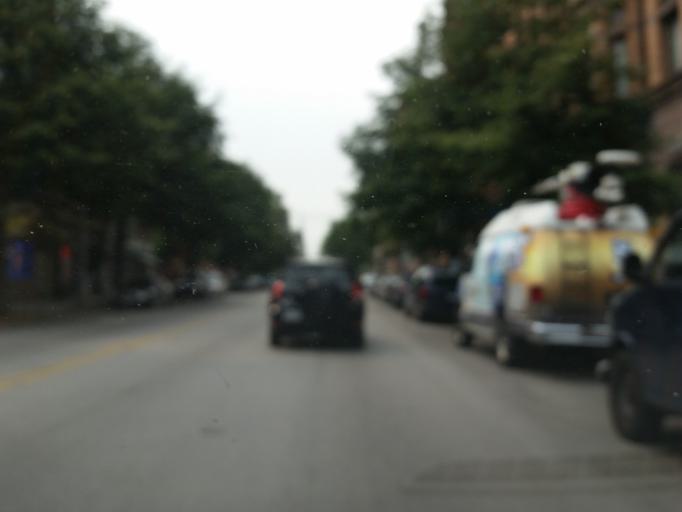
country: US
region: Pennsylvania
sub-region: York County
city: York
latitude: 39.9622
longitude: -76.7277
